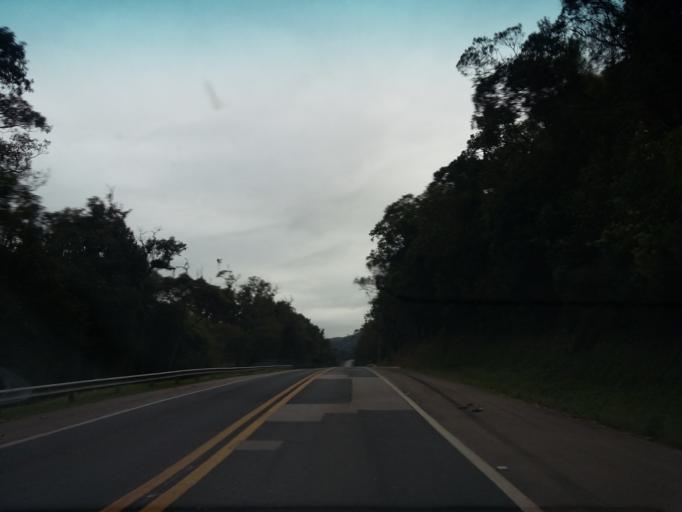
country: BR
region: Santa Catarina
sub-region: Santa Cecilia
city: Santa Cecilia
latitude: -26.7274
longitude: -50.3114
